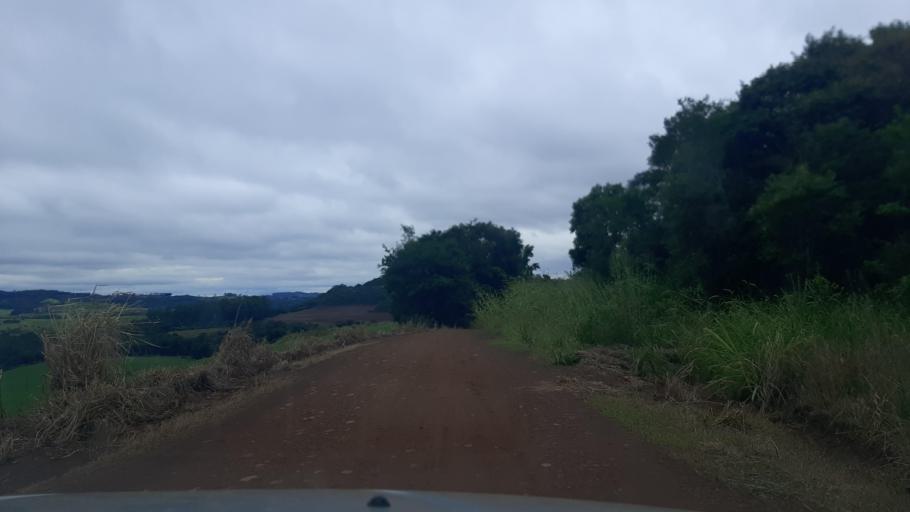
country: BR
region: Parana
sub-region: Ampere
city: Ampere
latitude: -26.0477
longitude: -53.5539
